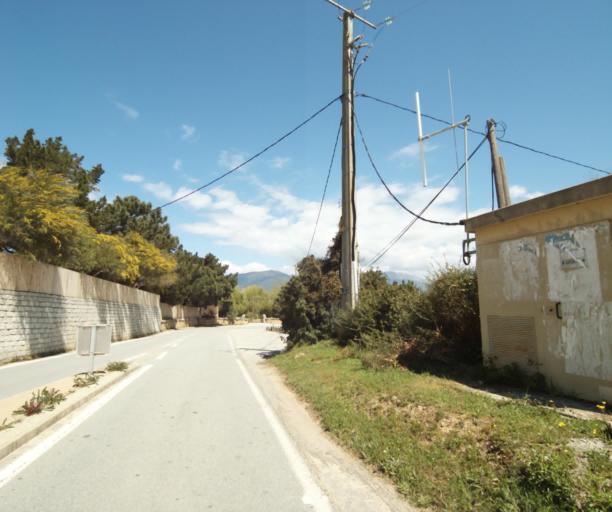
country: FR
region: Corsica
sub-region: Departement de la Corse-du-Sud
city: Propriano
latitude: 41.6442
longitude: 8.8688
